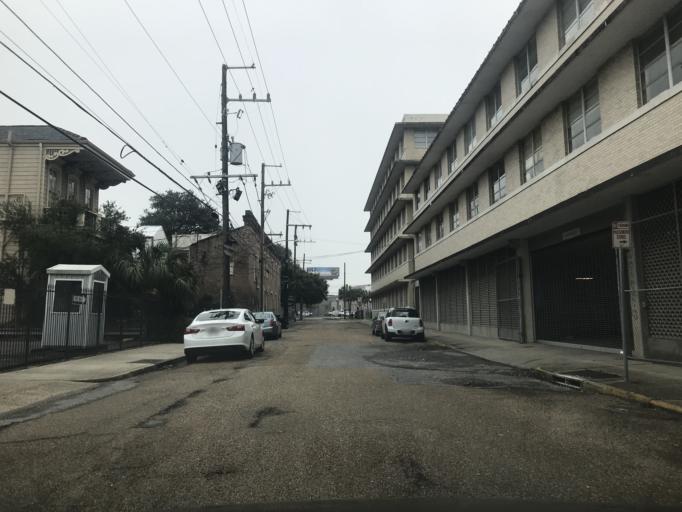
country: US
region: Louisiana
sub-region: Orleans Parish
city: New Orleans
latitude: 29.9411
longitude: -90.0733
